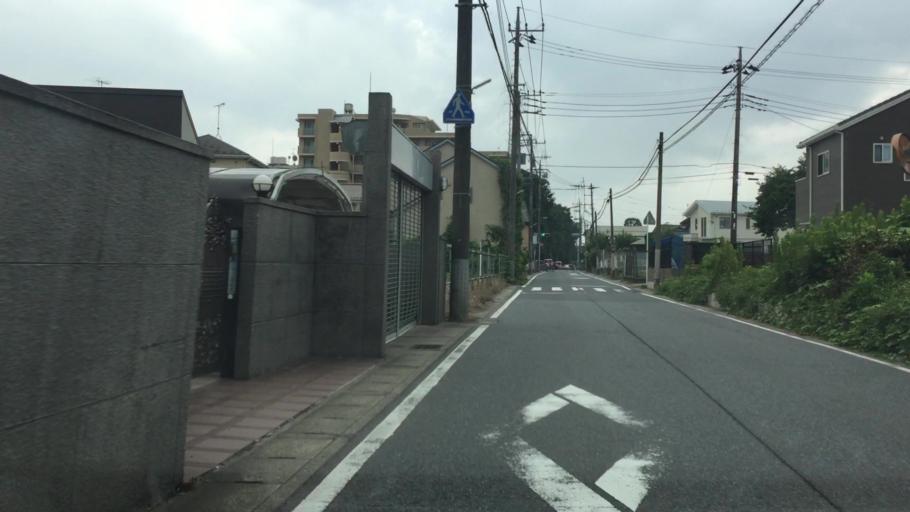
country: JP
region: Chiba
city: Kashiwa
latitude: 35.8065
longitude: 139.9496
